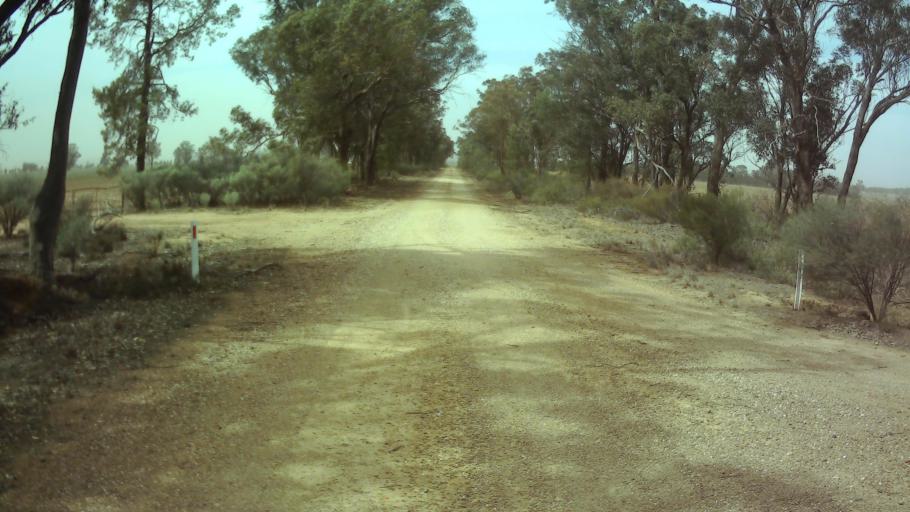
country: AU
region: New South Wales
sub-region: Weddin
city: Grenfell
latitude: -33.7121
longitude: 147.9702
